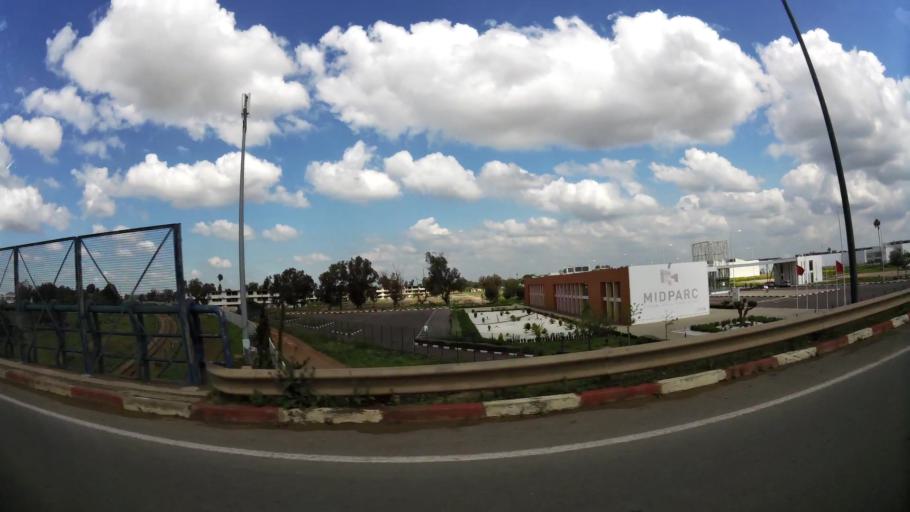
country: MA
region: Chaouia-Ouardigha
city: Nouaseur
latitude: 33.3768
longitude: -7.5687
